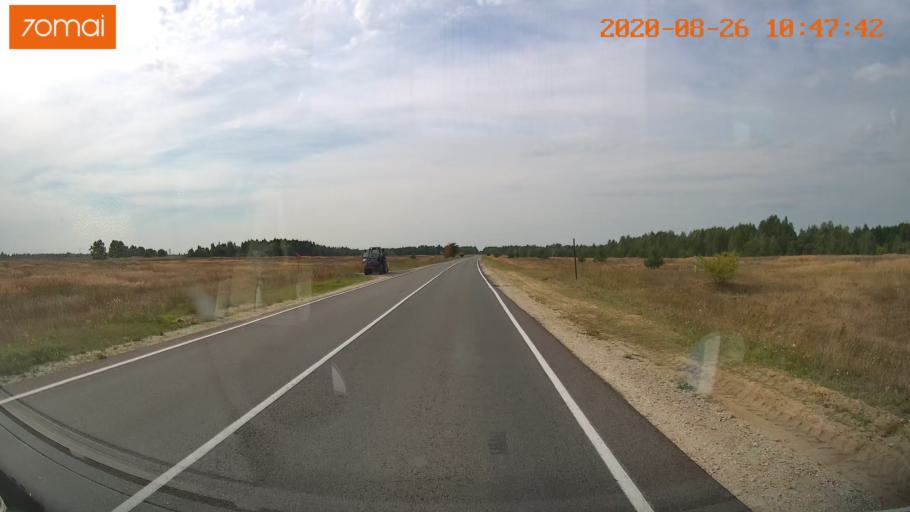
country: RU
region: Rjazan
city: Lashma
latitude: 54.7235
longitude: 41.1858
